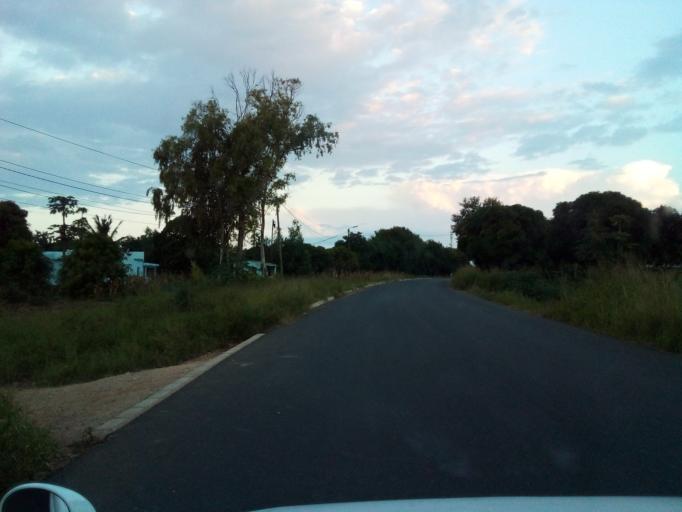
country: MZ
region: Maputo City
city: Maputo
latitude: -26.3399
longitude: 32.6713
